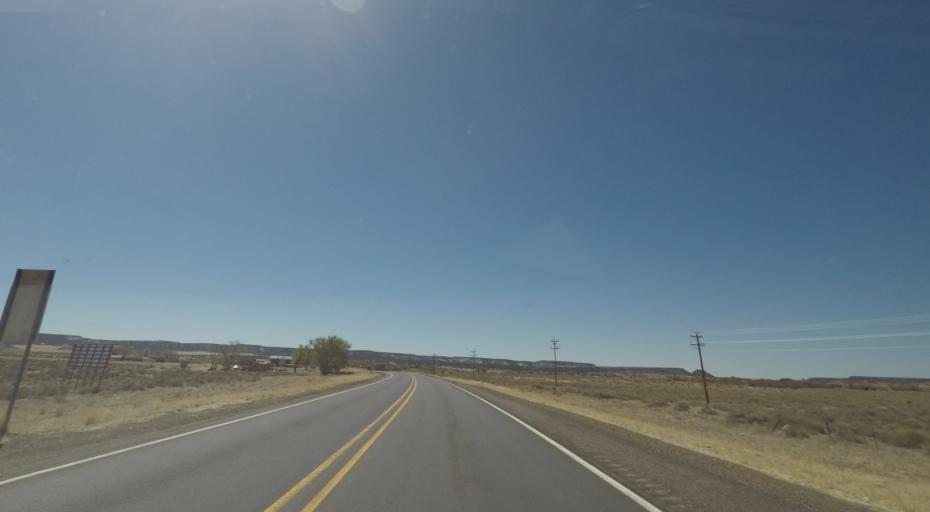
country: US
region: New Mexico
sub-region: Catron County
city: Reserve
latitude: 34.3443
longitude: -108.5019
